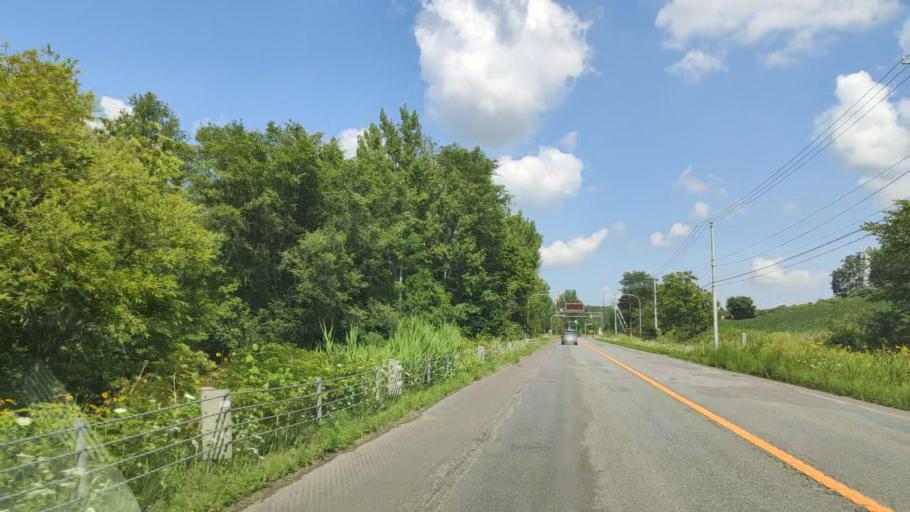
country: JP
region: Hokkaido
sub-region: Asahikawa-shi
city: Asahikawa
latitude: 43.5782
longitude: 142.4389
